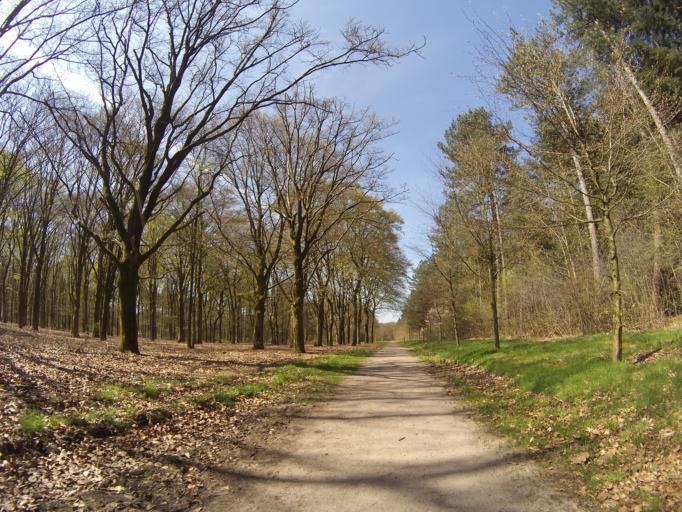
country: NL
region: Utrecht
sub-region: Gemeente Utrechtse Heuvelrug
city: Driebergen-Rijsenburg
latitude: 52.0831
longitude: 5.3144
